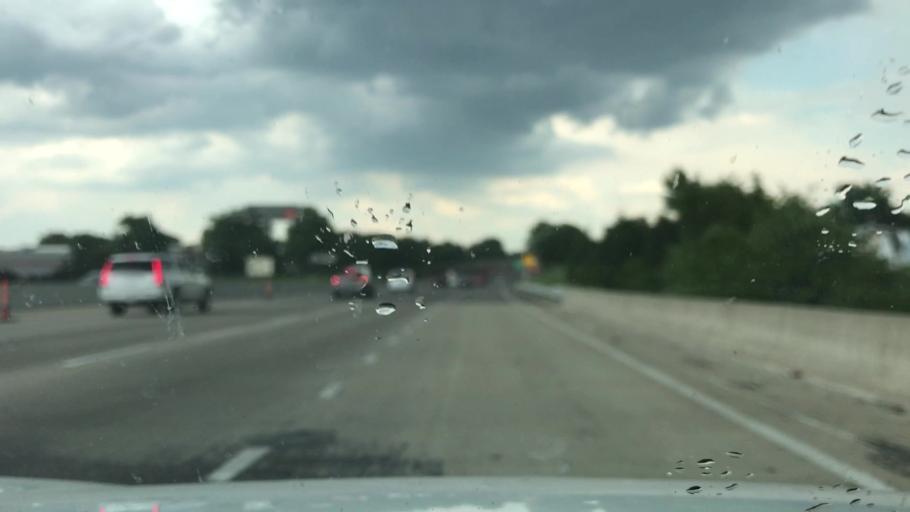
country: US
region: Missouri
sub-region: Saint Louis County
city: Richmond Heights
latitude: 38.6190
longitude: -90.2811
